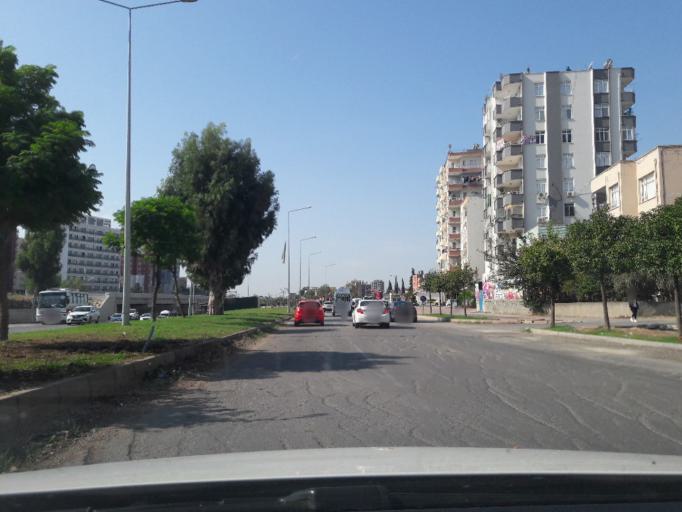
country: TR
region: Adana
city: Adana
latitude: 37.0050
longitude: 35.3168
